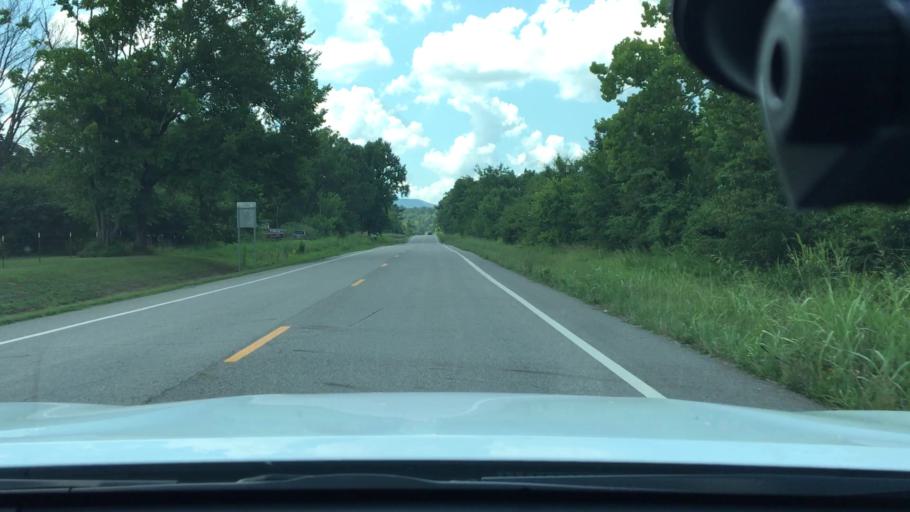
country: US
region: Arkansas
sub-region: Logan County
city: Paris
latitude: 35.2674
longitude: -93.6832
